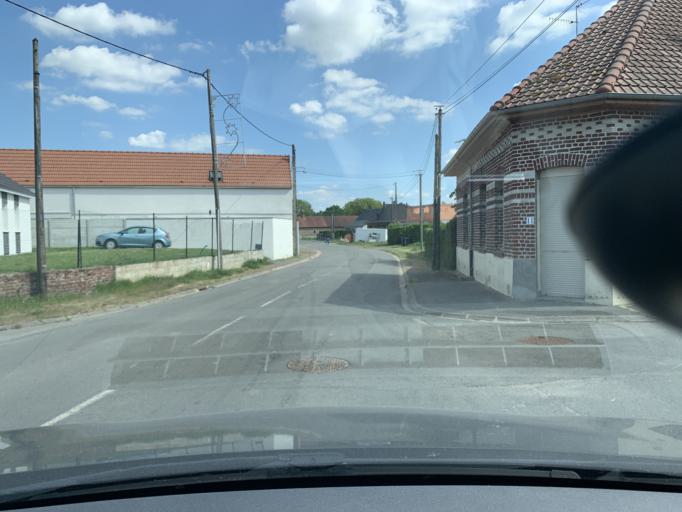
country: FR
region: Nord-Pas-de-Calais
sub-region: Departement du Pas-de-Calais
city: Marquion
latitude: 50.2348
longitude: 3.0933
